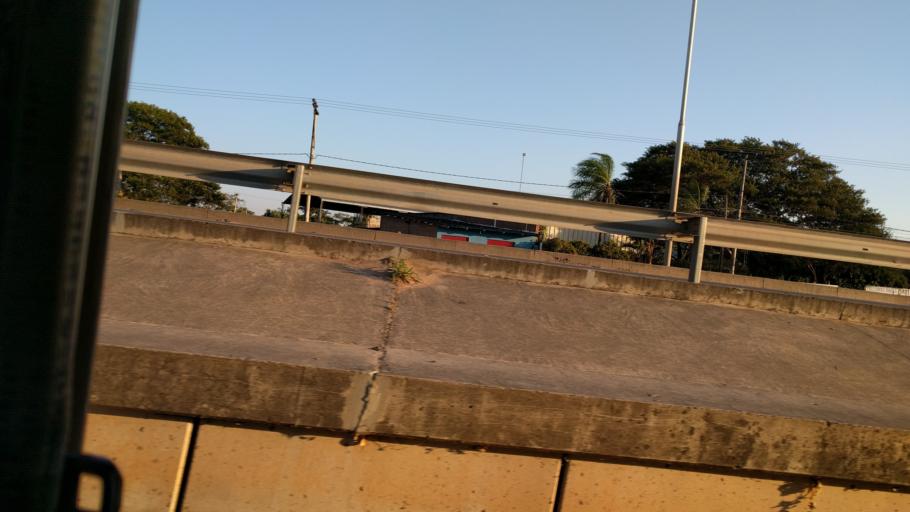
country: BO
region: Santa Cruz
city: Cotoca
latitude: -17.7650
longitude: -63.0854
